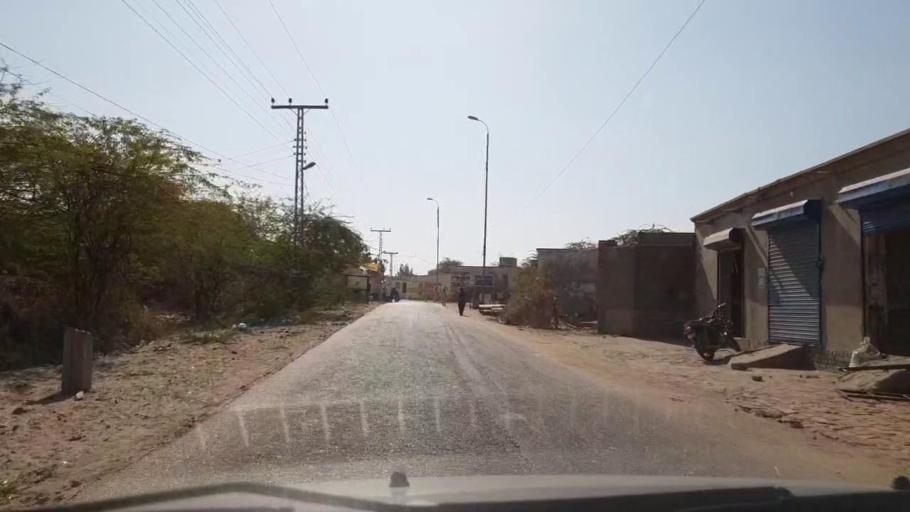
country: PK
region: Sindh
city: Diplo
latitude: 24.4719
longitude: 69.5795
